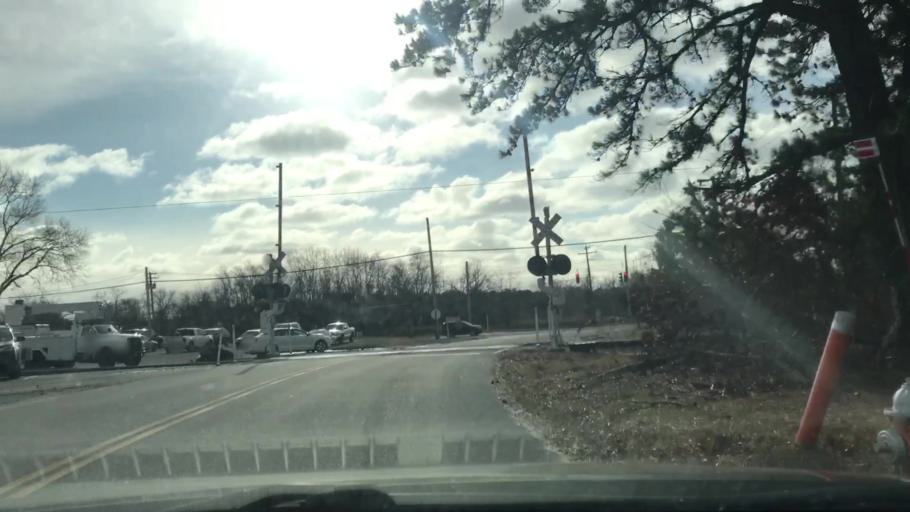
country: US
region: New York
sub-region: Suffolk County
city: Calverton
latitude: 40.9168
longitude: -72.7067
